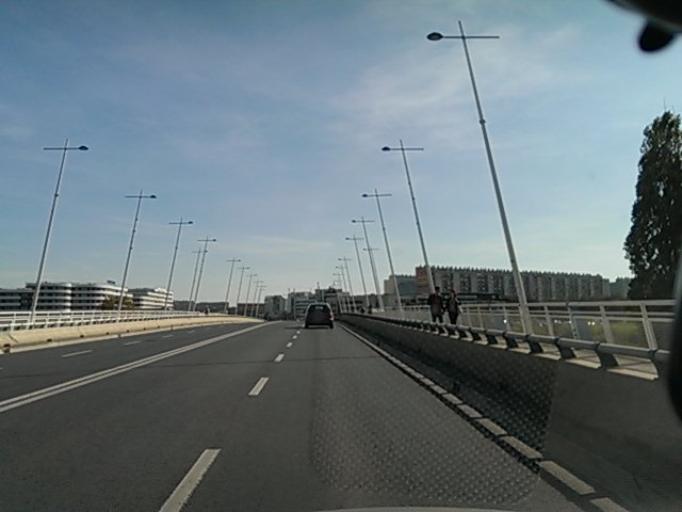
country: PL
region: Subcarpathian Voivodeship
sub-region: Rzeszow
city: Rzeszow
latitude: 50.0308
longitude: 22.0041
